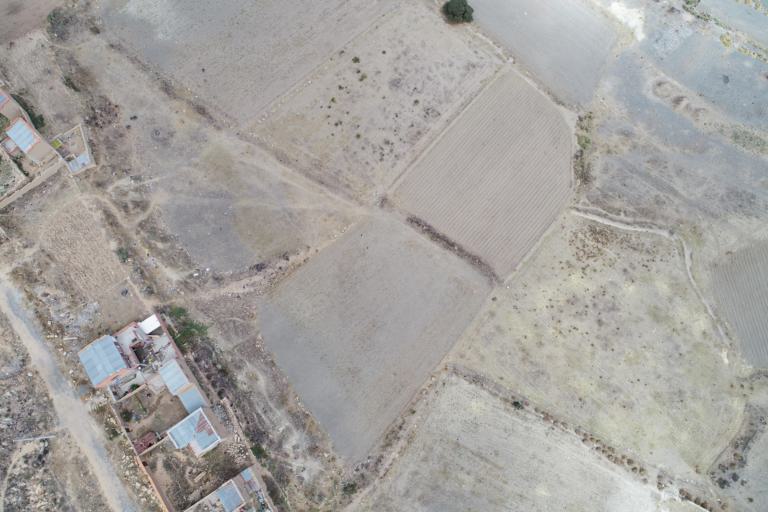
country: BO
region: La Paz
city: Achacachi
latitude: -16.0416
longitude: -68.6804
